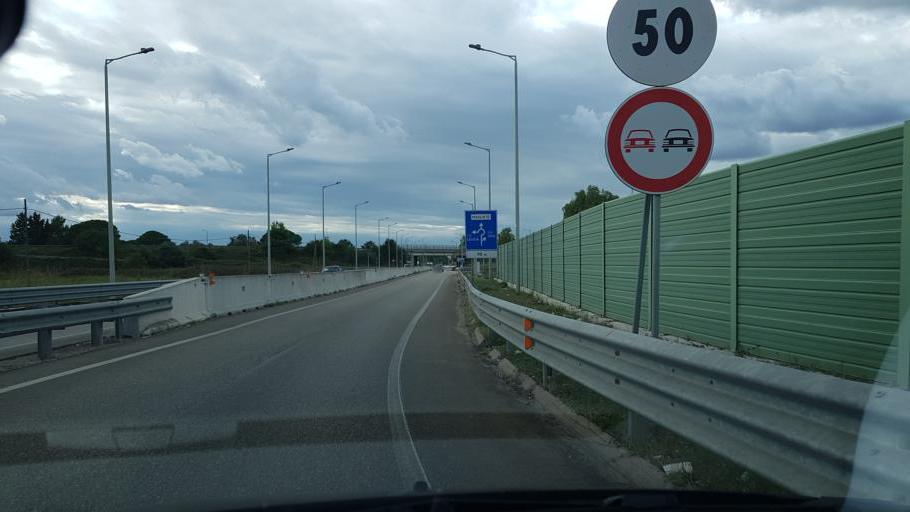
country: IT
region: Apulia
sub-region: Provincia di Lecce
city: Maglie
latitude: 40.1230
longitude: 18.3184
